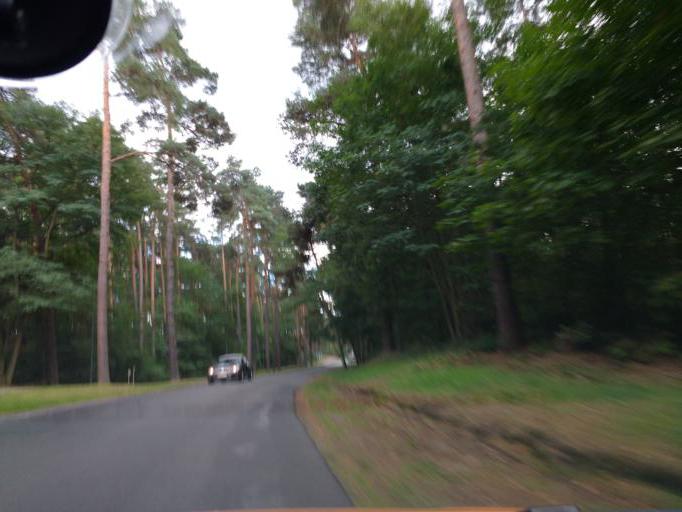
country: DE
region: Brandenburg
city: Bad Saarow
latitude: 52.2782
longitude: 14.0396
